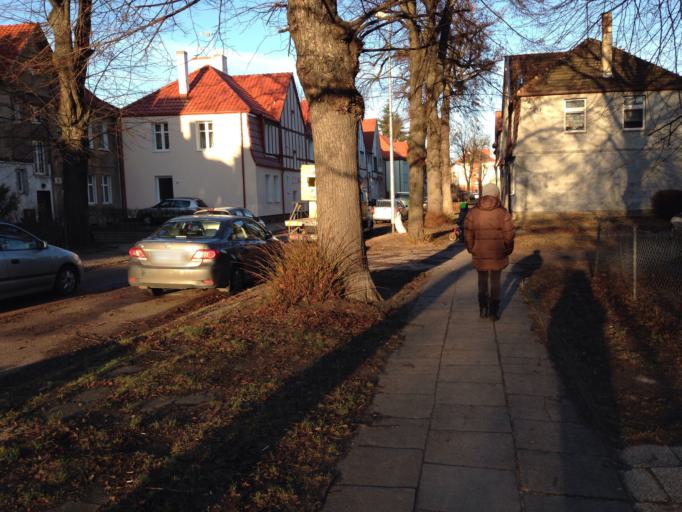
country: PL
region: Pomeranian Voivodeship
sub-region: Gdansk
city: Gdansk
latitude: 54.3842
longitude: 18.6280
